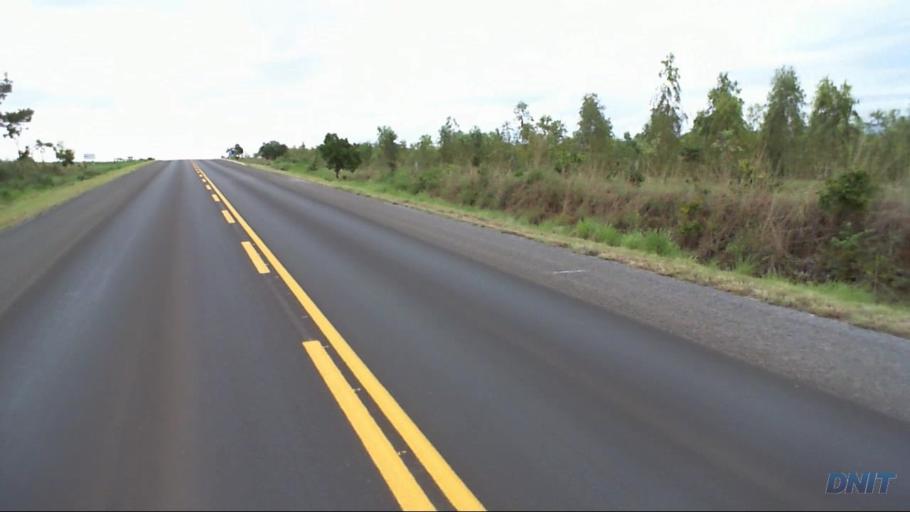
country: BR
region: Goias
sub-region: Barro Alto
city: Barro Alto
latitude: -15.2143
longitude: -48.6598
